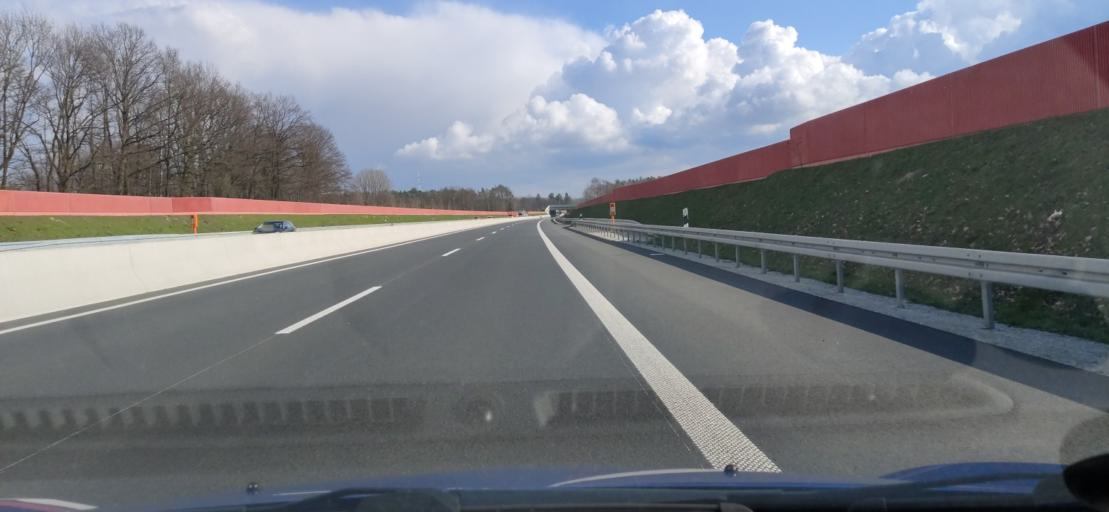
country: DE
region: North Rhine-Westphalia
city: Borgholzhausen
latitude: 52.0638
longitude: 8.3177
